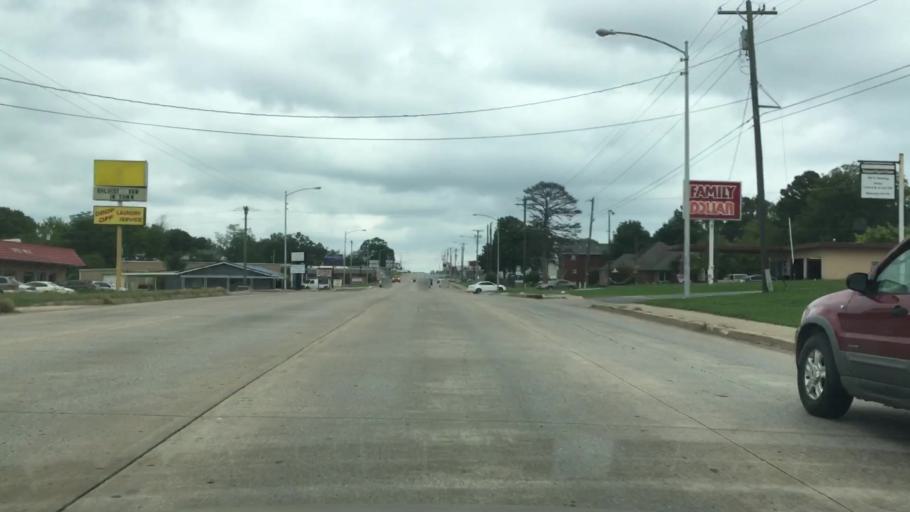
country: US
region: Oklahoma
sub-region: Cherokee County
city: Tahlequah
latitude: 35.9153
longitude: -94.9657
